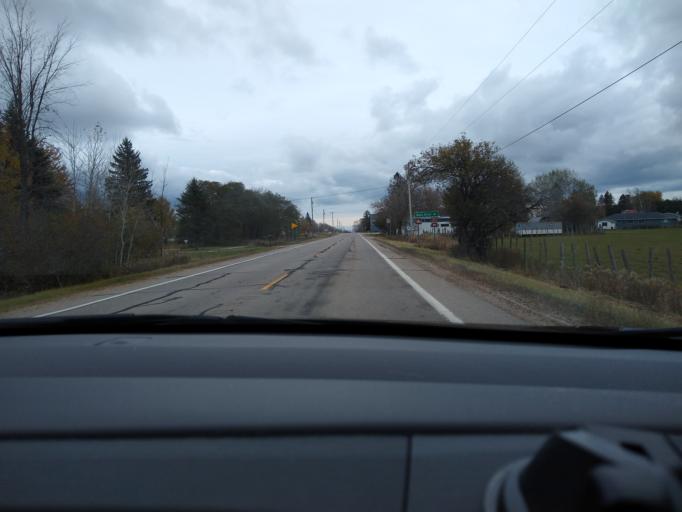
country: US
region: Michigan
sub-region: Delta County
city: Escanaba
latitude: 45.7634
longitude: -87.3016
